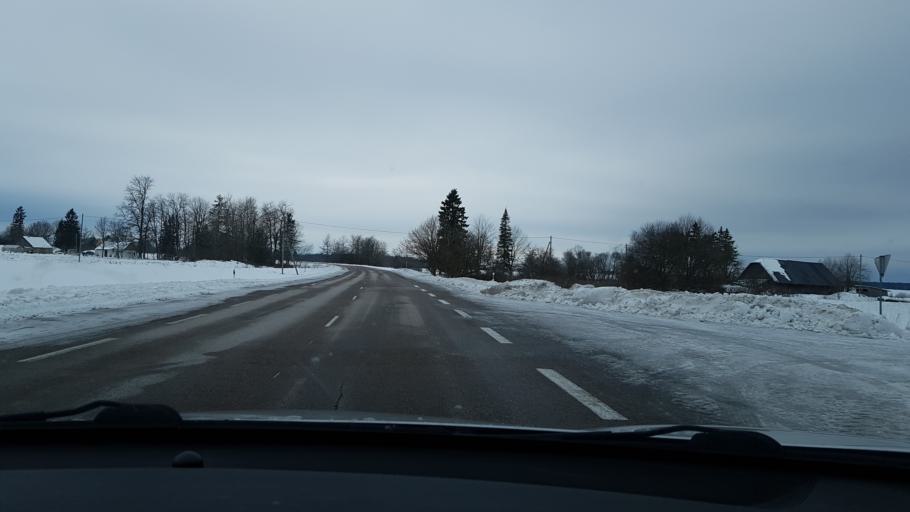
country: EE
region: Jaervamaa
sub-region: Jaerva-Jaani vald
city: Jarva-Jaani
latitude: 58.9052
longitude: 25.8198
